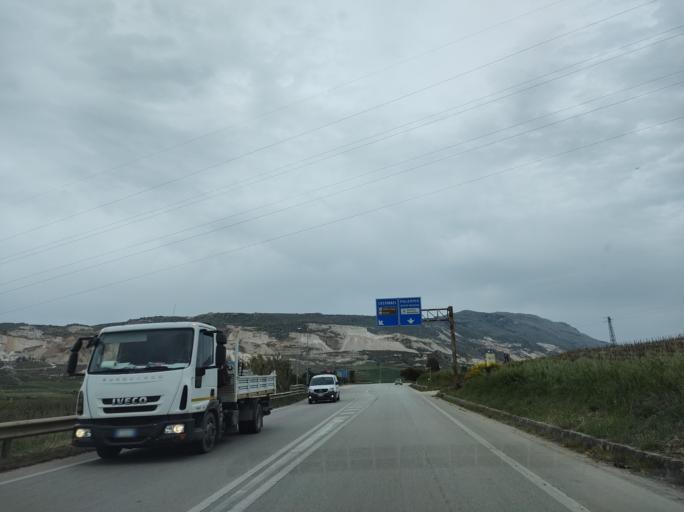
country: IT
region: Sicily
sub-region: Trapani
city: Custonaci
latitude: 38.0426
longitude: 12.6853
